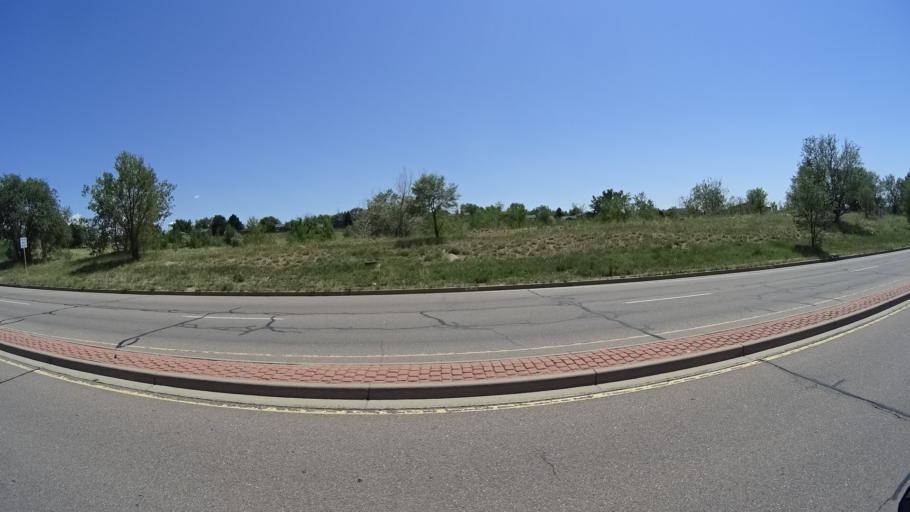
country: US
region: Colorado
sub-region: El Paso County
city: Security-Widefield
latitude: 38.7713
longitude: -104.7391
